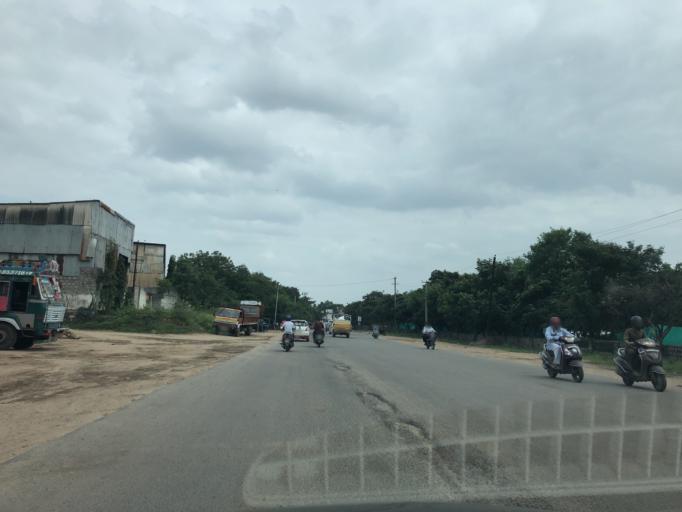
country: IN
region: Telangana
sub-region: Rangareddi
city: Quthbullapur
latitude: 17.4718
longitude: 78.4746
